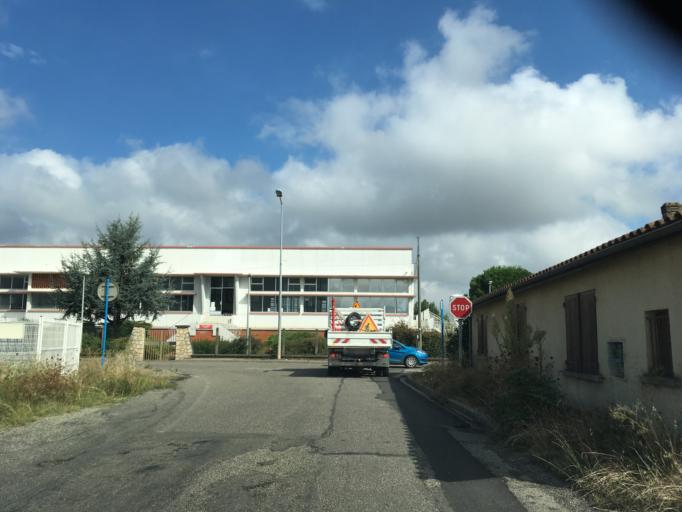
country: FR
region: Aquitaine
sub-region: Departement du Lot-et-Garonne
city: Boe
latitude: 44.1790
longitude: 0.6220
